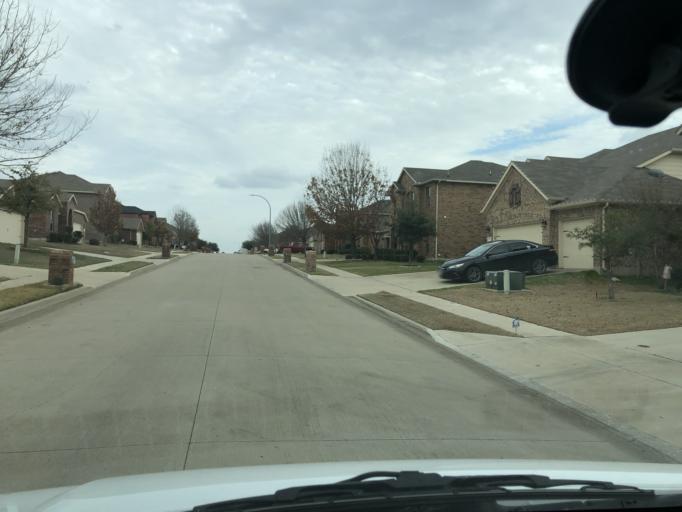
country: US
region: Texas
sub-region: Tarrant County
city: Saginaw
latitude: 32.9067
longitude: -97.3702
